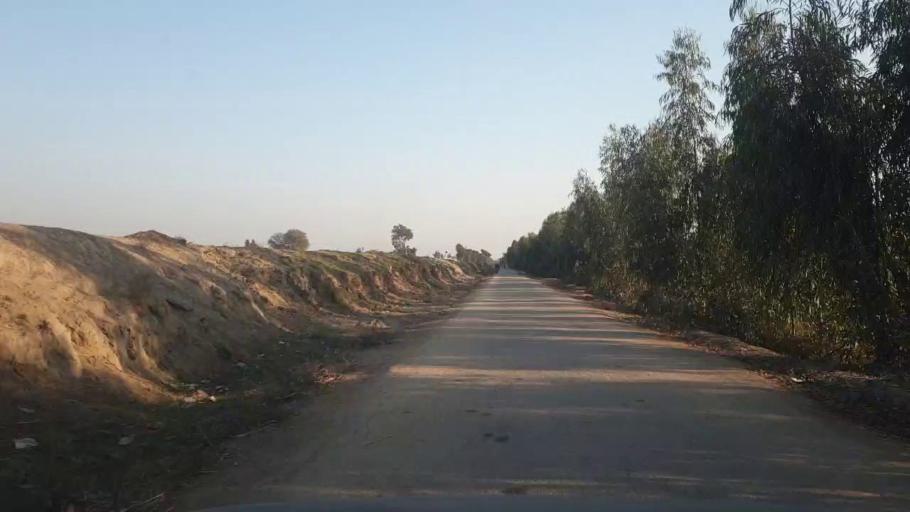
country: PK
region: Sindh
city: Chambar
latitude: 25.2922
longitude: 68.8940
